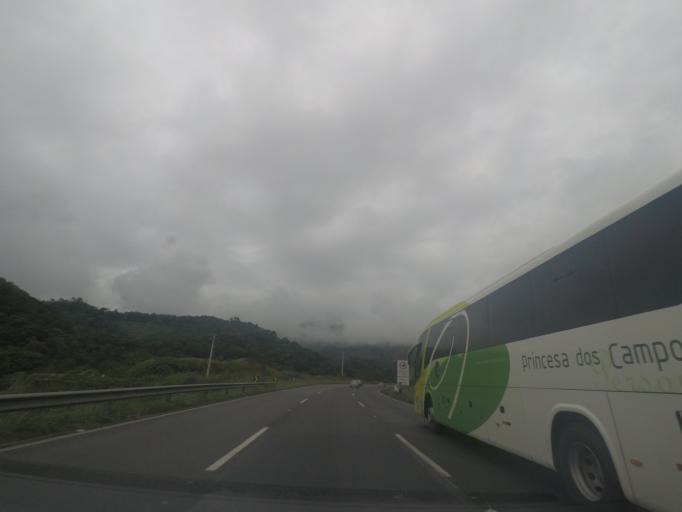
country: BR
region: Sao Paulo
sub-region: Cajati
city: Cajati
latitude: -24.8714
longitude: -48.2163
